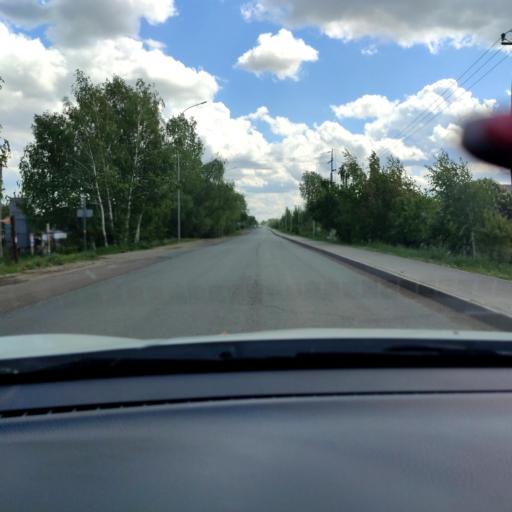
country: RU
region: Tatarstan
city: Stolbishchi
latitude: 55.6991
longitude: 49.1844
